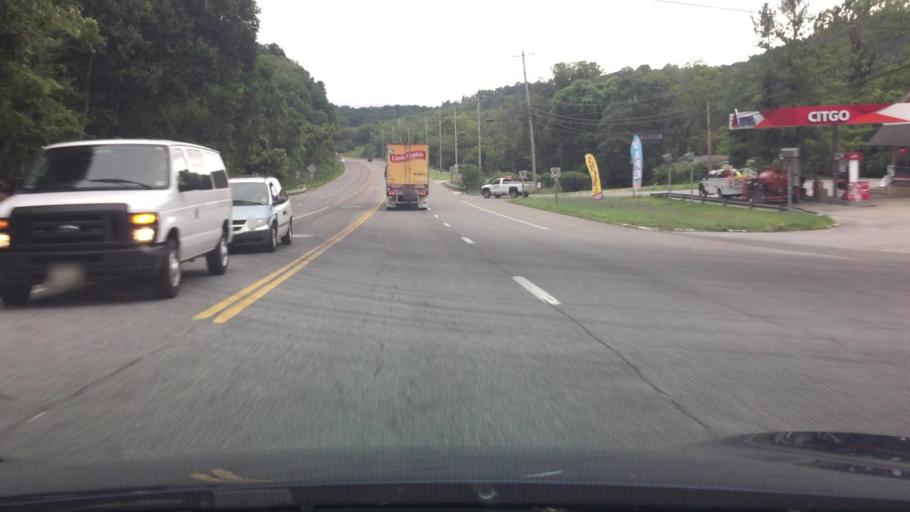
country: US
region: Virginia
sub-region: Montgomery County
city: Shawsville
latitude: 37.2462
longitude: -80.1762
